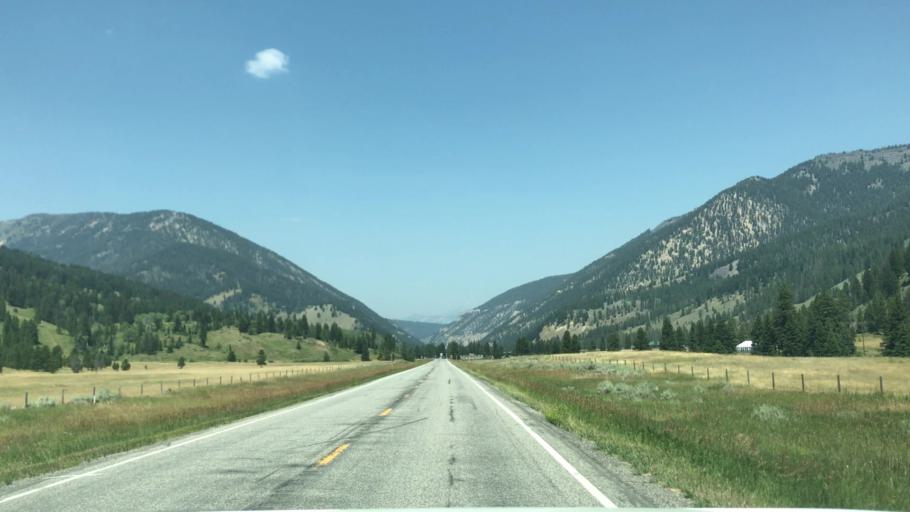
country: US
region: Montana
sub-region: Gallatin County
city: Big Sky
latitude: 45.0943
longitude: -111.2150
